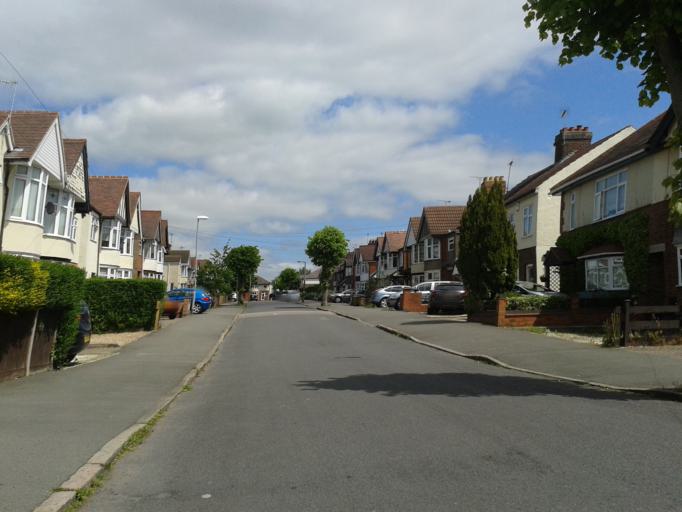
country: GB
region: England
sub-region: Leicestershire
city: Hinckley
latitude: 52.5419
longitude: -1.3568
